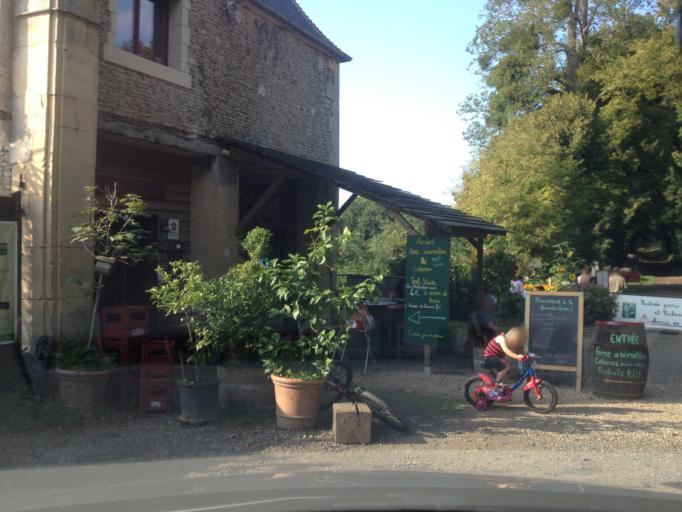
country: FR
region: Lower Normandy
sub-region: Departement du Calvados
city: Canon
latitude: 49.0802
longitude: -0.0938
